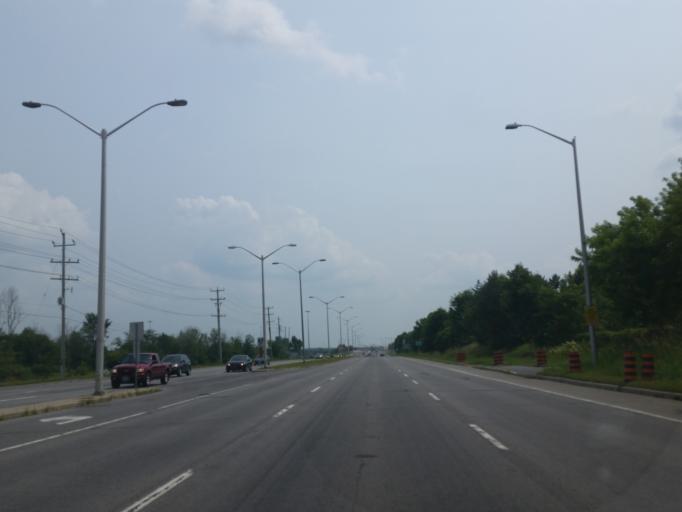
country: CA
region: Ontario
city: Bells Corners
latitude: 45.3266
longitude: -75.8898
